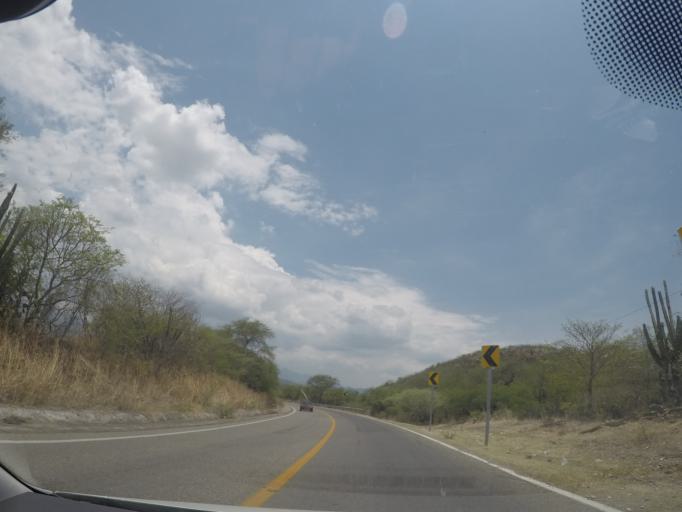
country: MX
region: Oaxaca
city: Magdalena Tequisistlan
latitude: 16.4281
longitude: -95.5424
